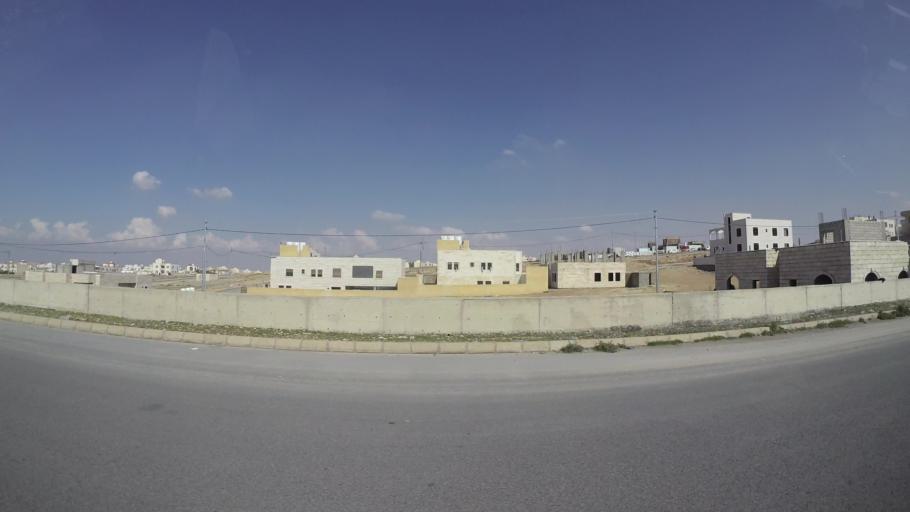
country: JO
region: Zarqa
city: Zarqa
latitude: 32.0516
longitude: 36.1145
